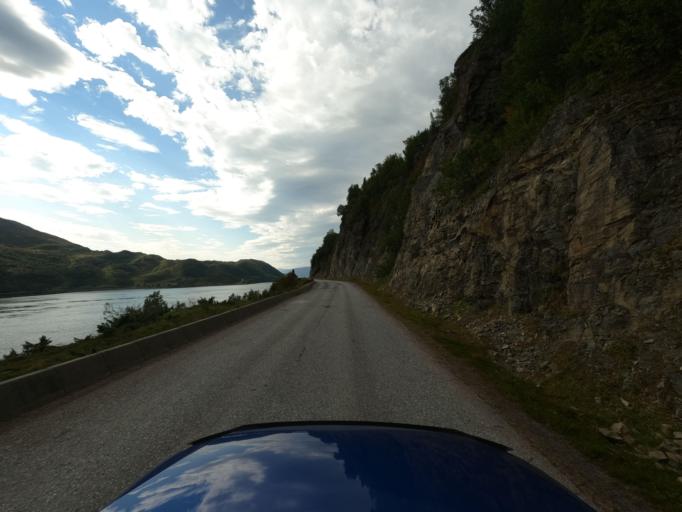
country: NO
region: Finnmark Fylke
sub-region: Kvalsund
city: Kvalsund
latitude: 70.5107
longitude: 23.9195
